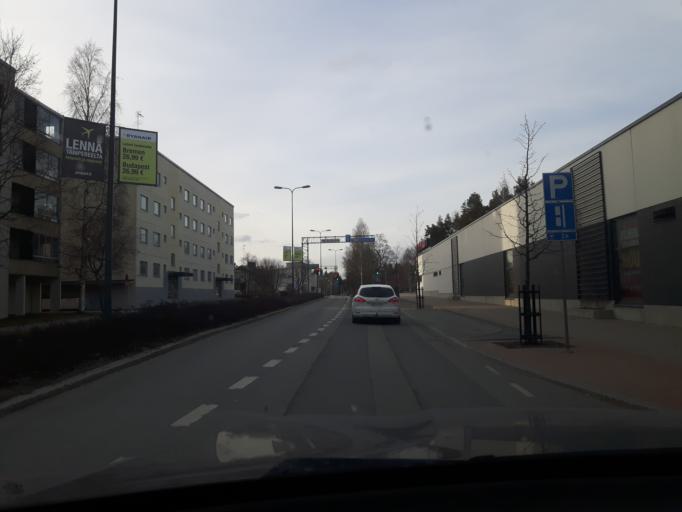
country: FI
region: Pirkanmaa
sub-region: Etelae-Pirkanmaa
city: Valkeakoski
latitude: 61.2677
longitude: 24.0311
